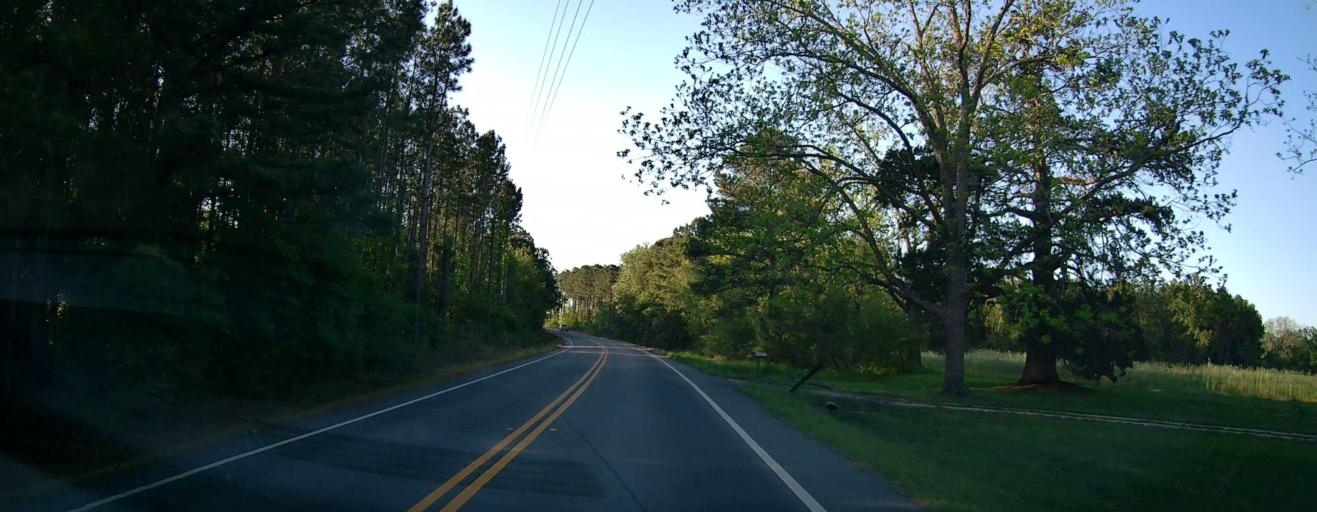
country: US
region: Georgia
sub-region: Ben Hill County
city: Fitzgerald
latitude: 31.6570
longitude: -83.1754
